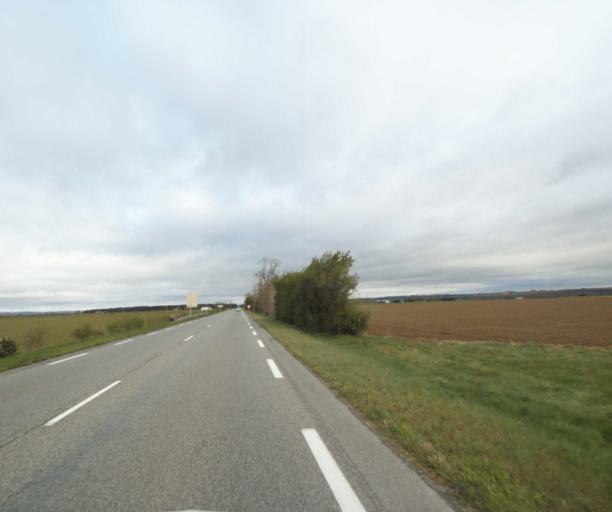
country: FR
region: Midi-Pyrenees
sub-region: Departement de l'Ariege
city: Saverdun
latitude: 43.2612
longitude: 1.5588
